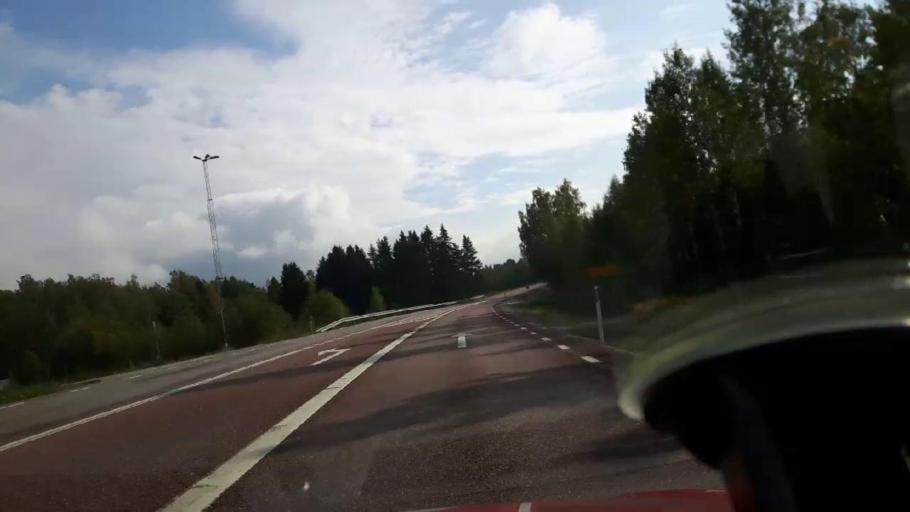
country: SE
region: Gaevleborg
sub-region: Bollnas Kommun
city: Kilafors
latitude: 61.2162
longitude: 16.7310
